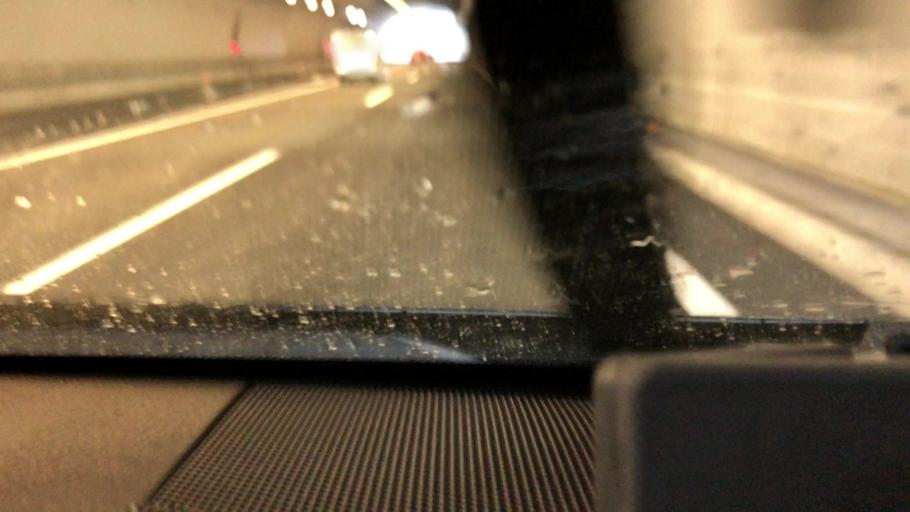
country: JP
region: Shizuoka
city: Mishima
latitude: 35.1994
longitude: 138.8884
